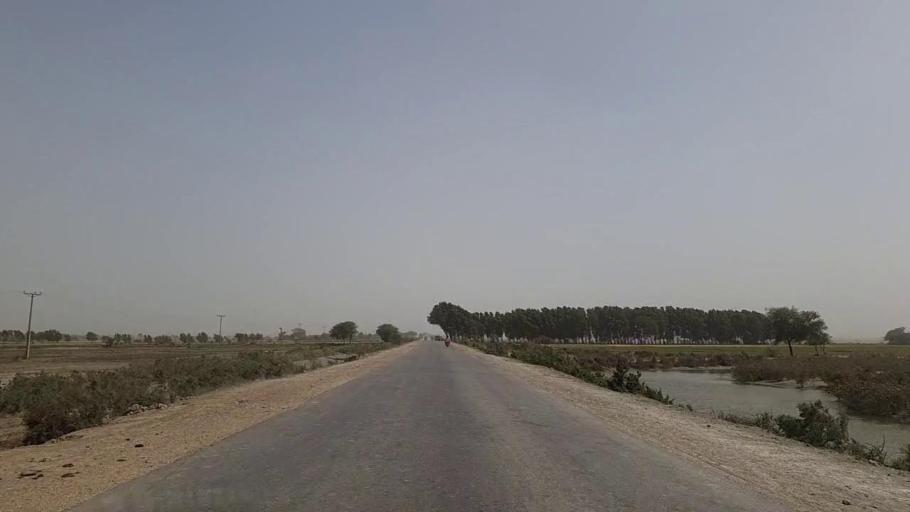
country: PK
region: Sindh
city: Talhar
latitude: 24.8804
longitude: 68.8313
